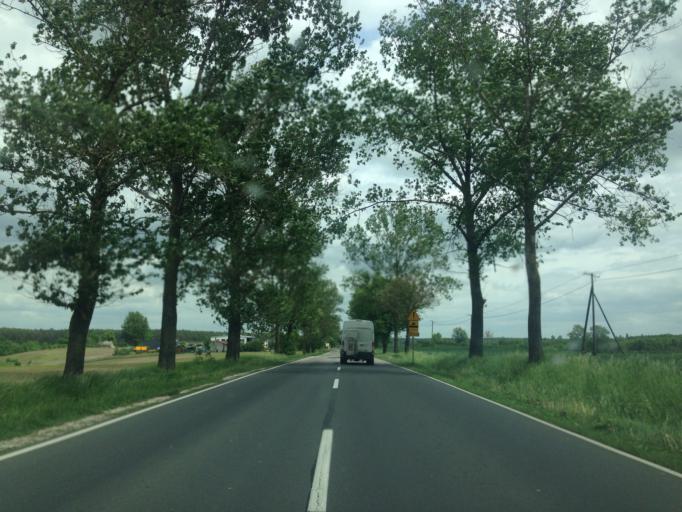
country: PL
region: Kujawsko-Pomorskie
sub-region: Powiat golubsko-dobrzynski
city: Golub-Dobrzyn
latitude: 53.1891
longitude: 19.0503
